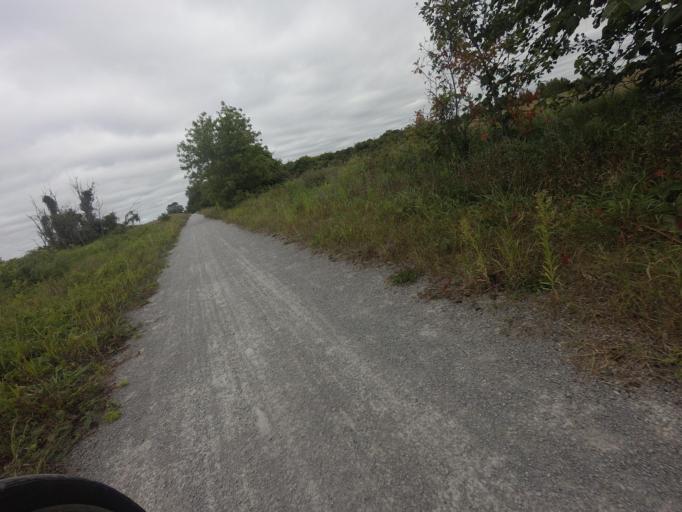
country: CA
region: Ontario
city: Omemee
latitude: 44.3294
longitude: -78.7736
